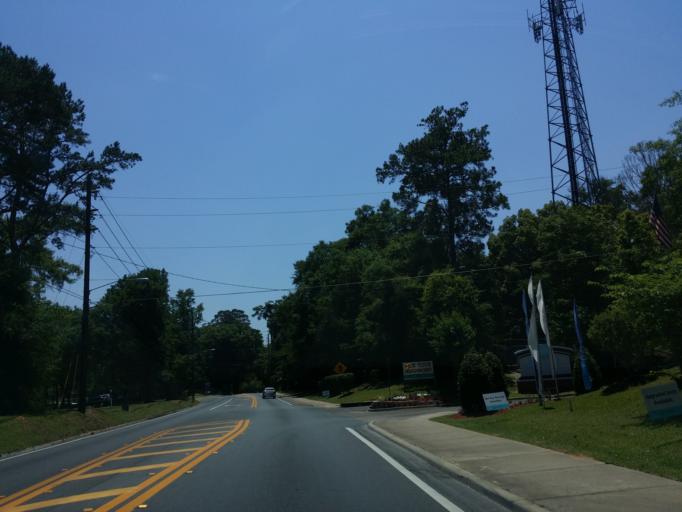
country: US
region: Florida
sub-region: Leon County
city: Tallahassee
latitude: 30.4602
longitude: -84.2968
